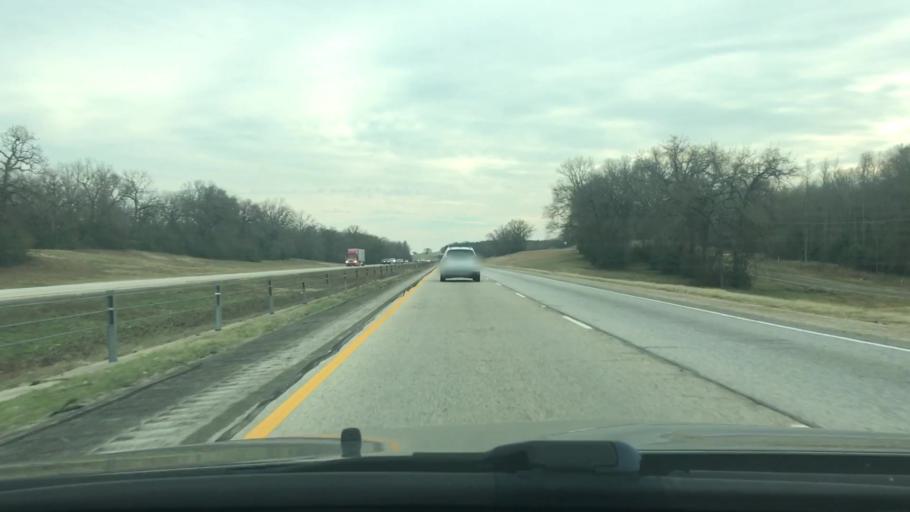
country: US
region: Texas
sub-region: Leon County
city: Centerville
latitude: 31.3038
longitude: -96.0008
